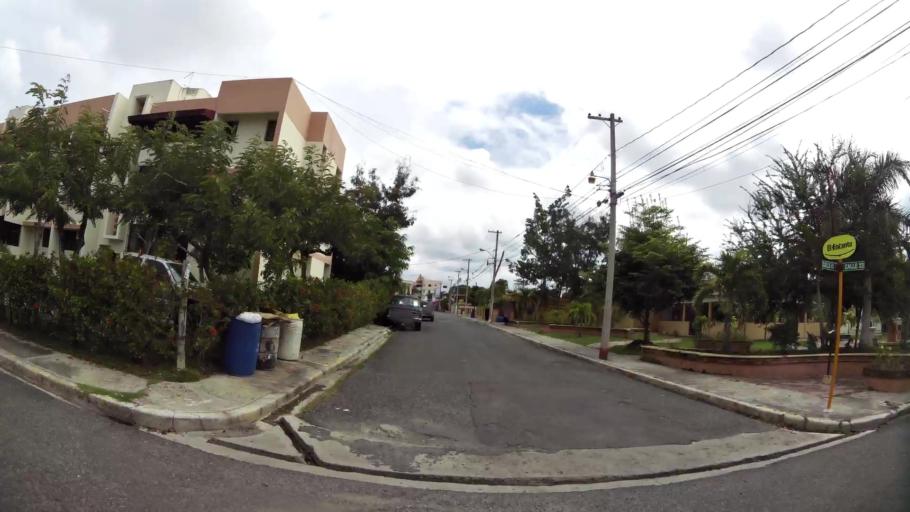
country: DO
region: Santiago
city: Santiago de los Caballeros
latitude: 19.4409
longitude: -70.6736
